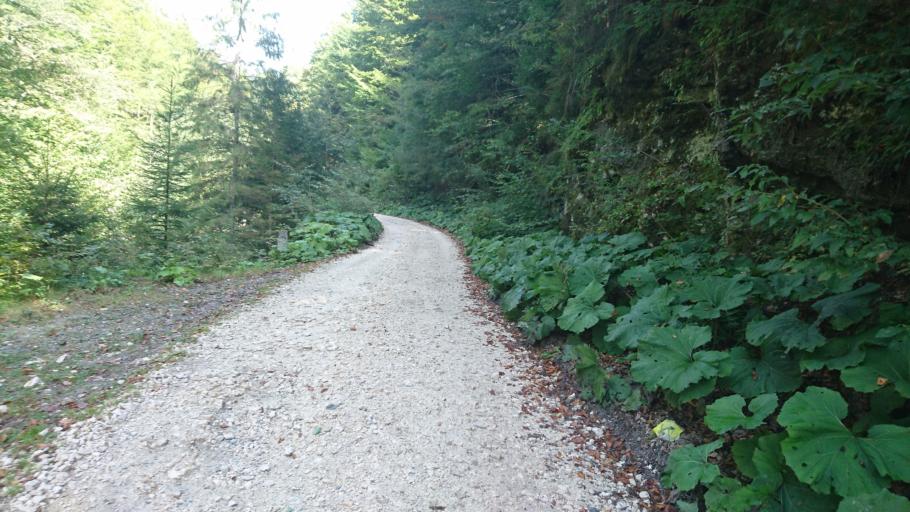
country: RO
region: Dambovita
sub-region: Comuna Pucheni
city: Pucheni
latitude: 45.2386
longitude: 25.3296
